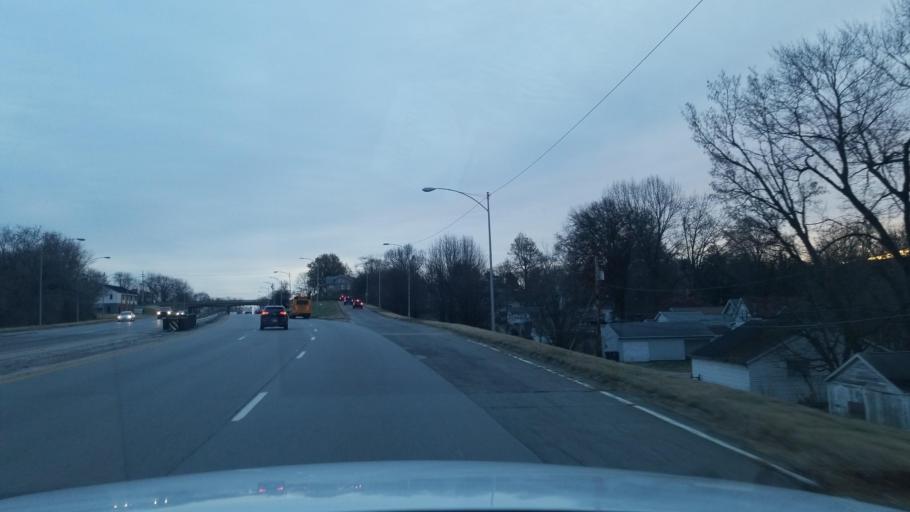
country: US
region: Indiana
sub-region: Vanderburgh County
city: Evansville
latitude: 37.9775
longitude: -87.6134
